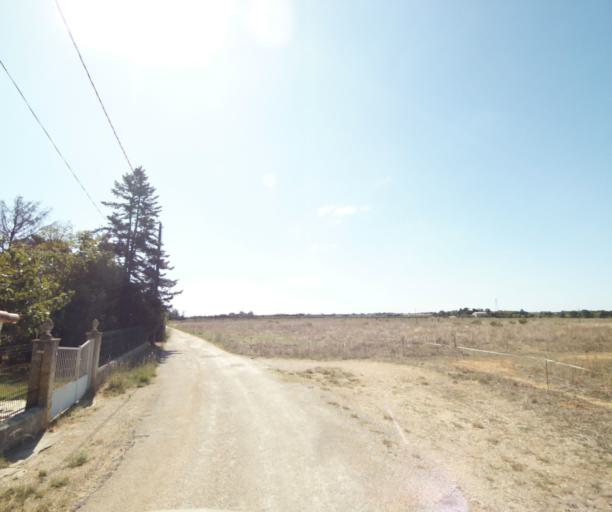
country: FR
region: Languedoc-Roussillon
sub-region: Departement du Gard
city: Rodilhan
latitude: 43.8179
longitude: 4.4359
